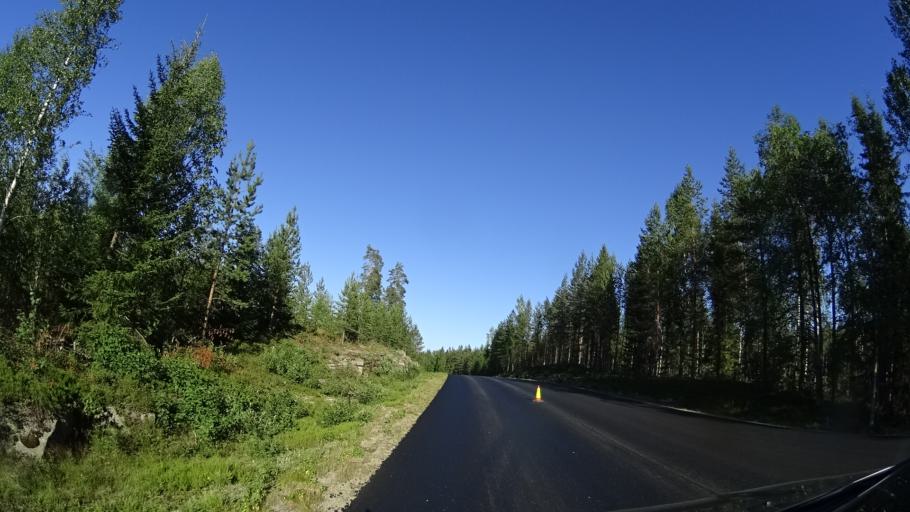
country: FI
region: North Karelia
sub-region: Pielisen Karjala
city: Valtimo
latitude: 63.5603
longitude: 28.5980
